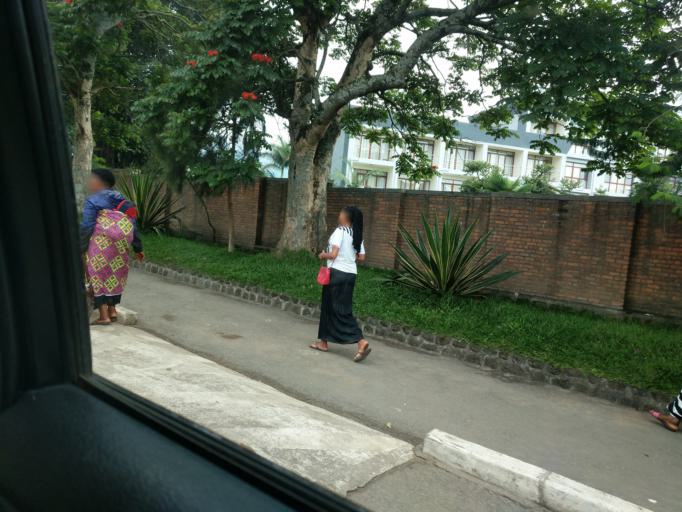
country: RW
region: Northern Province
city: Musanze
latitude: -1.5075
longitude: 29.6386
